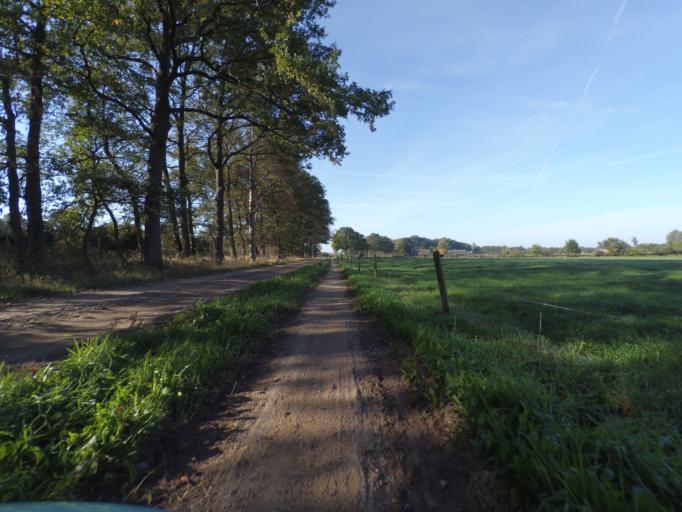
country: NL
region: Gelderland
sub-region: Berkelland
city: Eibergen
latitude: 52.0881
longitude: 6.6976
